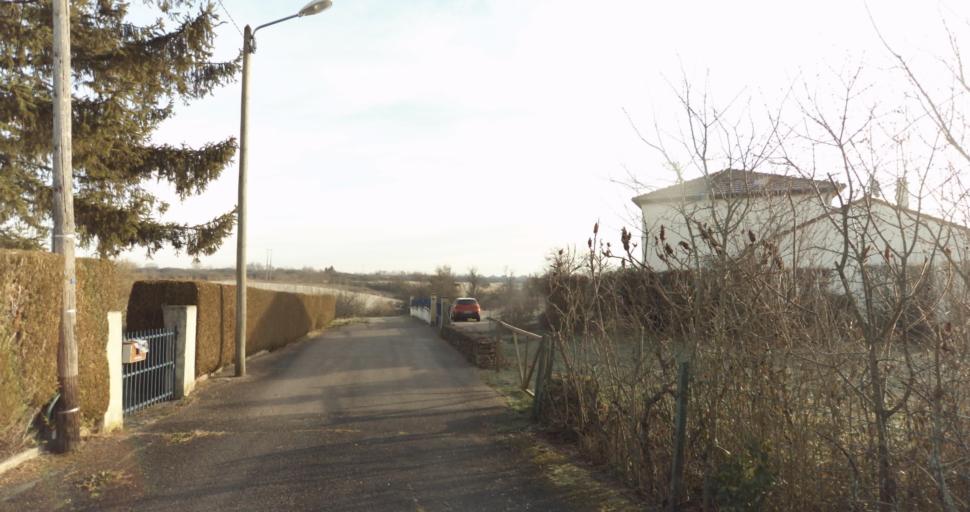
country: FR
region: Lorraine
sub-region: Departement de Meurthe-et-Moselle
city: Jarny
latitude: 49.1603
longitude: 5.8913
